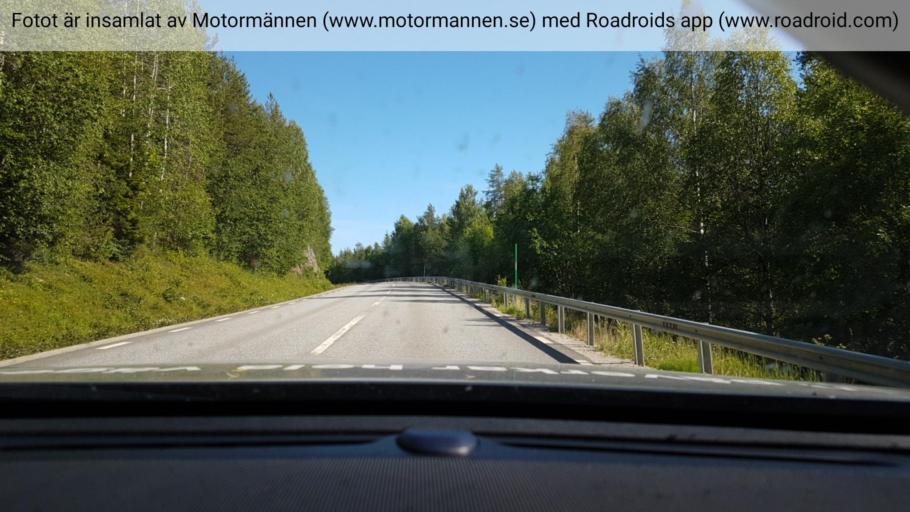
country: SE
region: Vaesterbotten
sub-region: Lycksele Kommun
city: Lycksele
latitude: 64.6541
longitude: 18.4572
